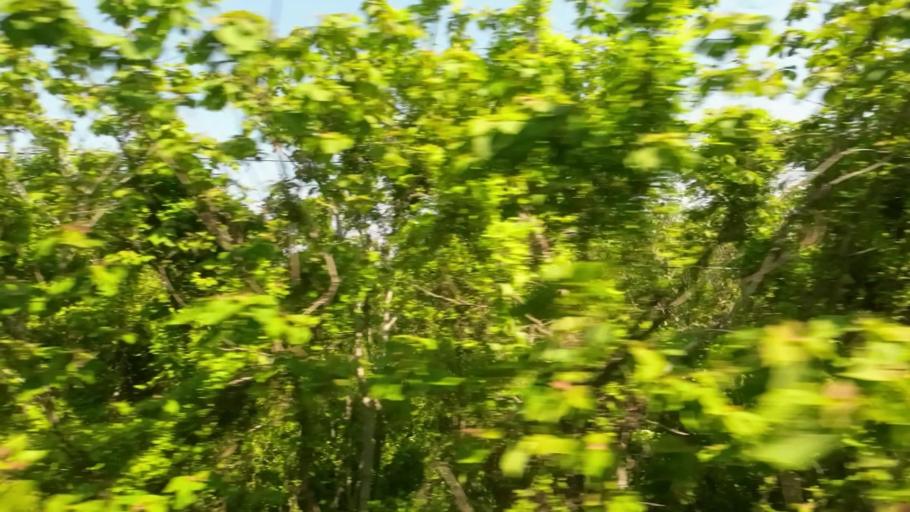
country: JP
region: Ehime
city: Kawanoecho
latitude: 33.9678
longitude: 133.4967
